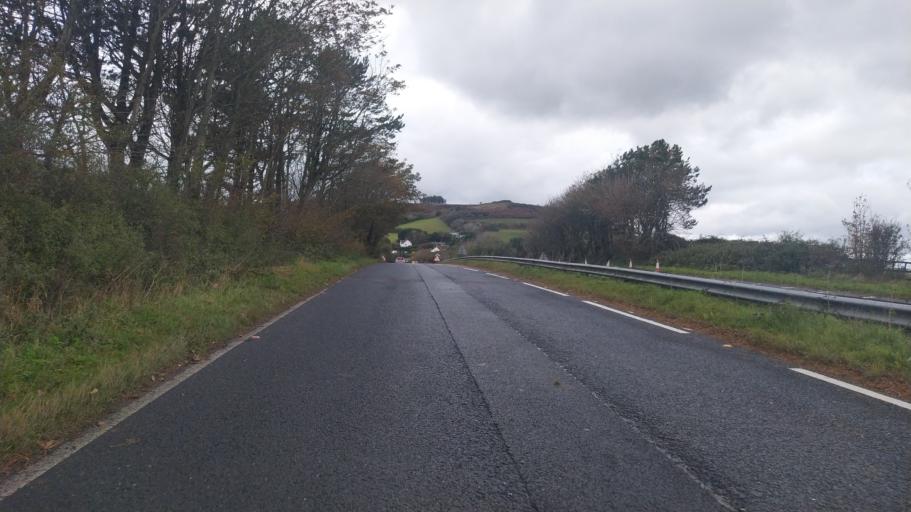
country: GB
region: England
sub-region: Dorset
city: Bridport
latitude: 50.7384
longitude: -2.8356
